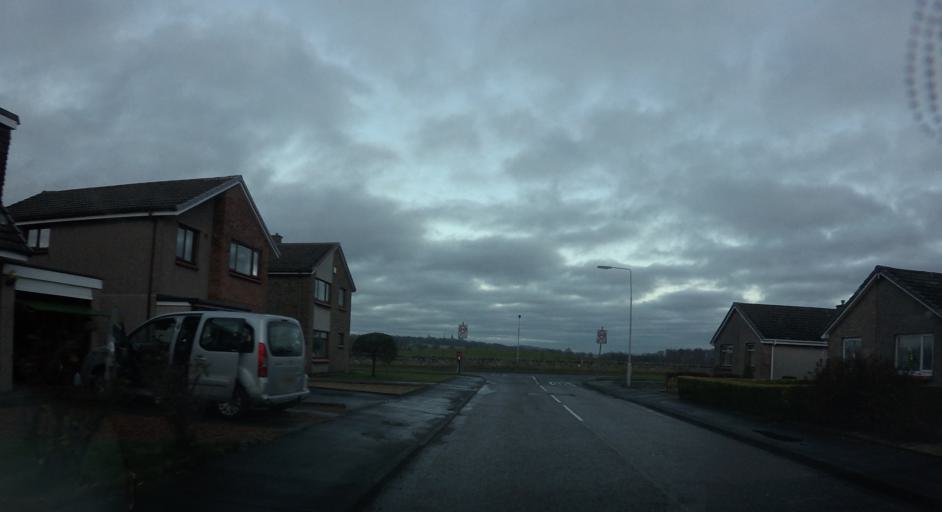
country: GB
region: Scotland
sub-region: Fife
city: Crossford
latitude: 56.0593
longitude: -3.4946
